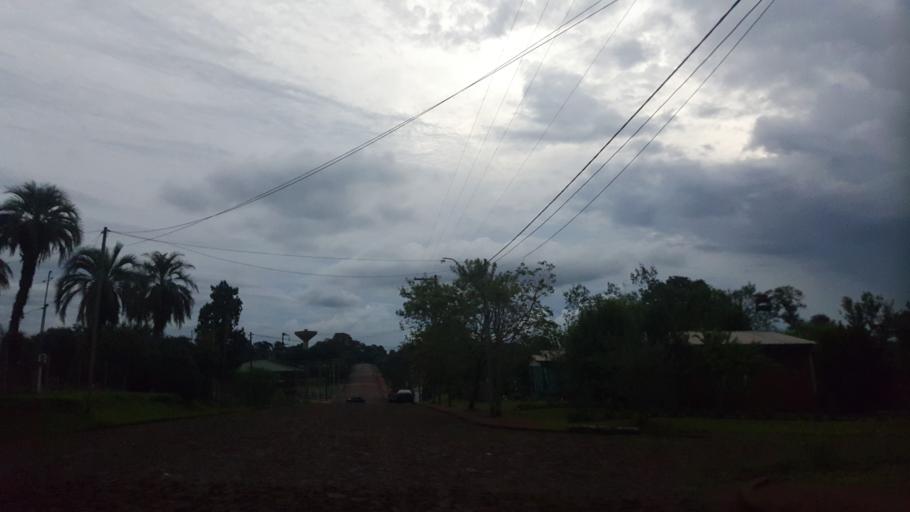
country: AR
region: Misiones
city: Capiovi
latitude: -26.9347
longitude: -55.0521
